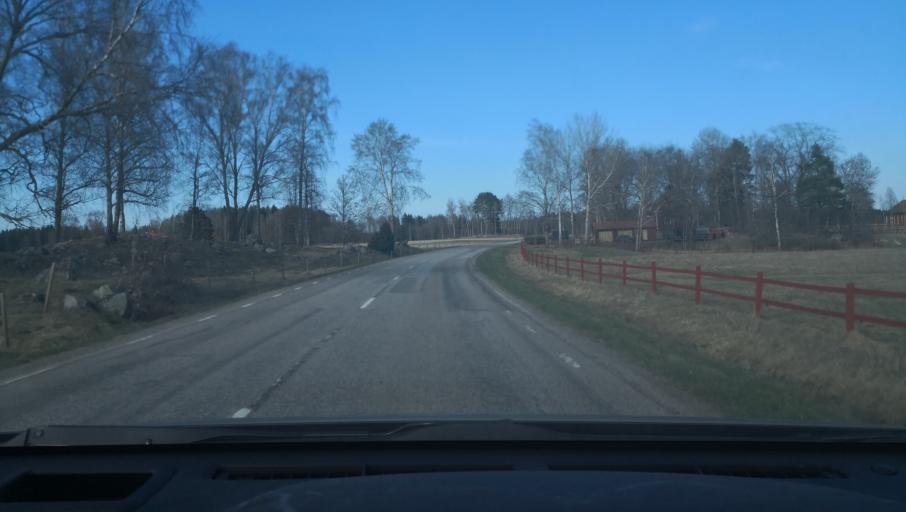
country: SE
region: Uppsala
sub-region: Heby Kommun
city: Heby
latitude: 59.9598
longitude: 16.8850
